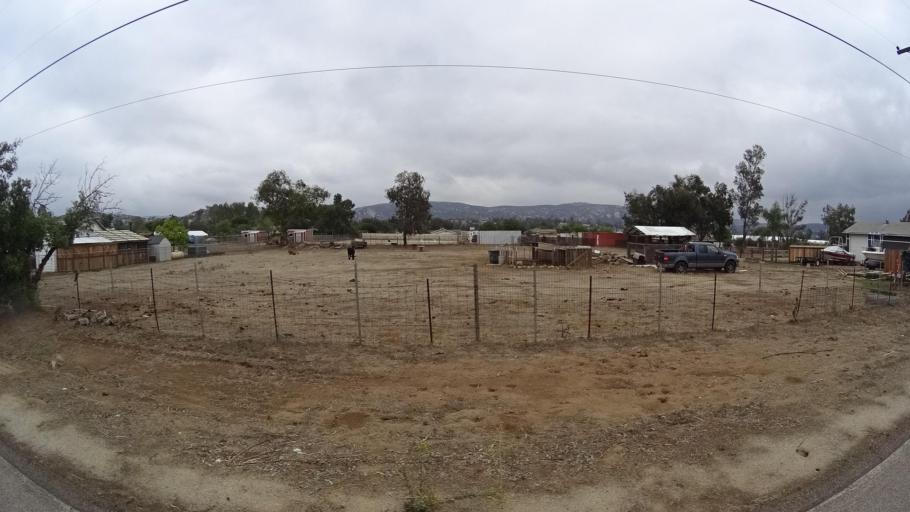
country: US
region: California
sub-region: San Diego County
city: Ramona
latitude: 33.0667
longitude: -116.8631
